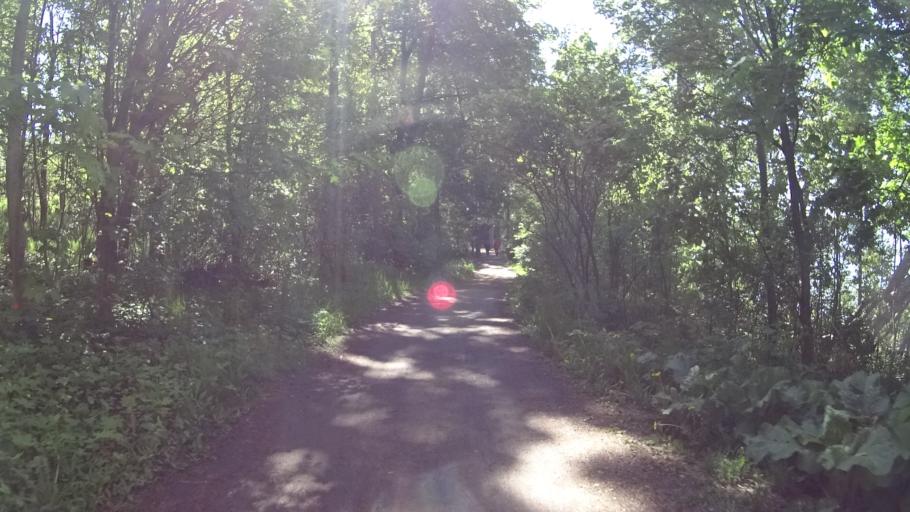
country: FI
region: Uusimaa
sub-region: Helsinki
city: Teekkarikylae
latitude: 60.1774
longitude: 24.8476
